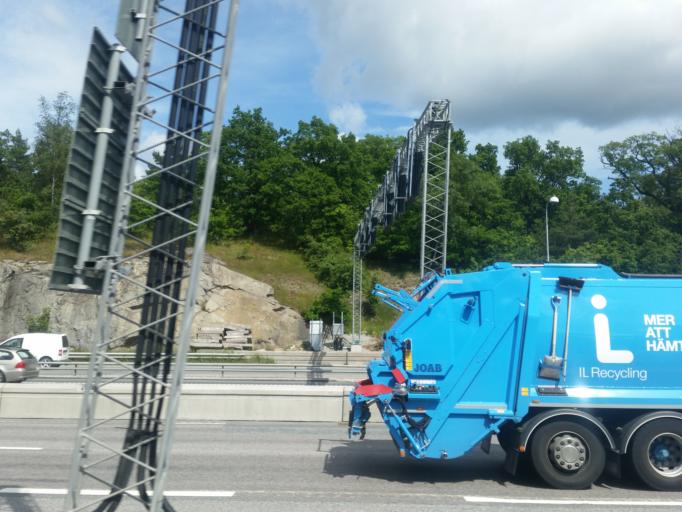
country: SE
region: Stockholm
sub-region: Norrtalje Kommun
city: Bergshamra
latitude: 59.3550
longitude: 18.0353
